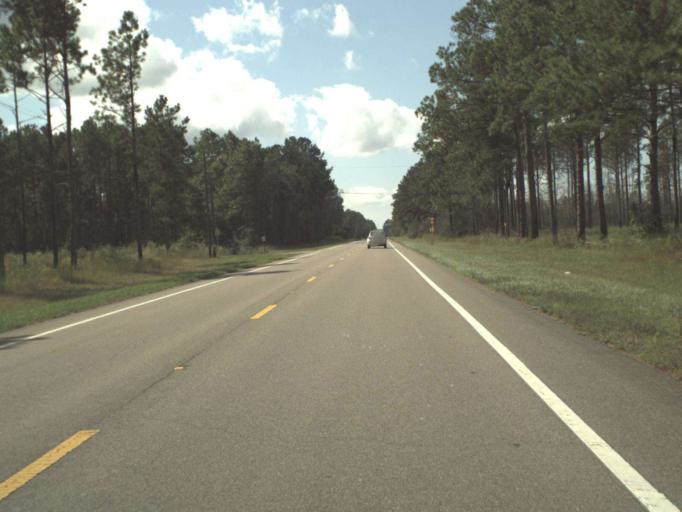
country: US
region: Florida
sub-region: Walton County
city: Freeport
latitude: 30.4914
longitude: -85.9395
